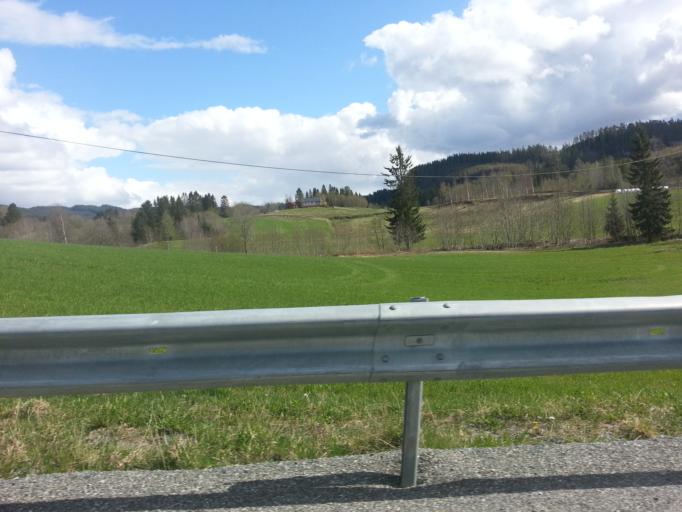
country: NO
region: Nord-Trondelag
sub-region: Levanger
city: Skogn
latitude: 63.6323
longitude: 11.2763
